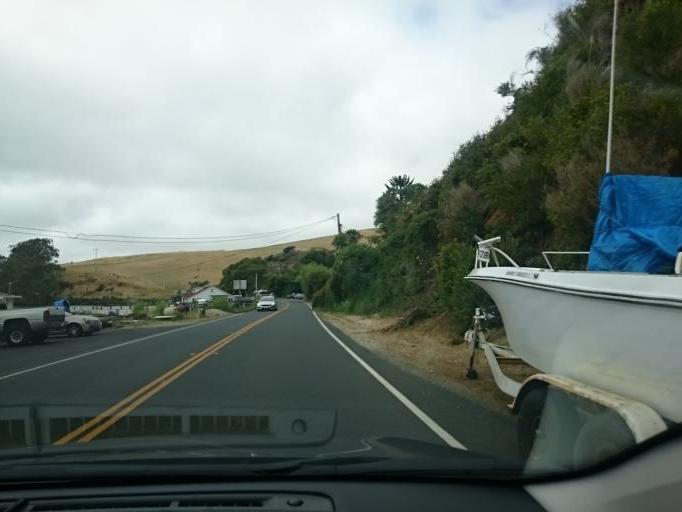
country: US
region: California
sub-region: Marin County
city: Inverness
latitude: 38.1471
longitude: -122.8829
